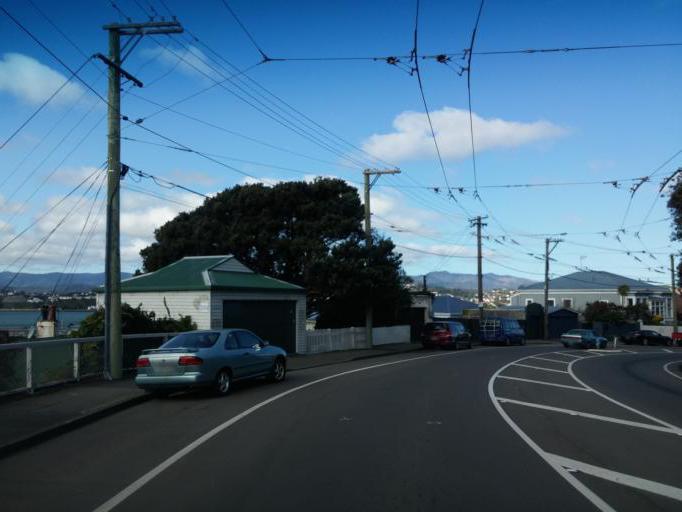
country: NZ
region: Wellington
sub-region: Wellington City
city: Wellington
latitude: -41.3140
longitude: 174.7906
